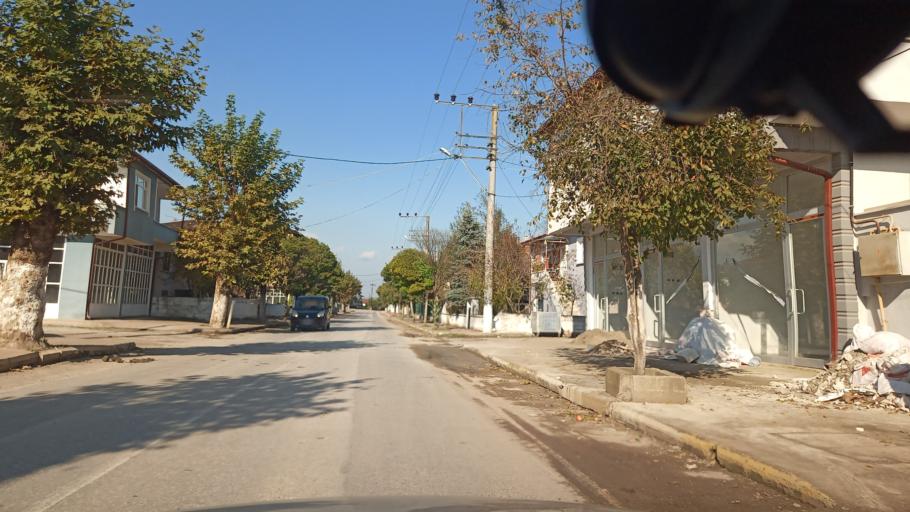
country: TR
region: Sakarya
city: Sogutlu
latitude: 40.9071
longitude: 30.4738
